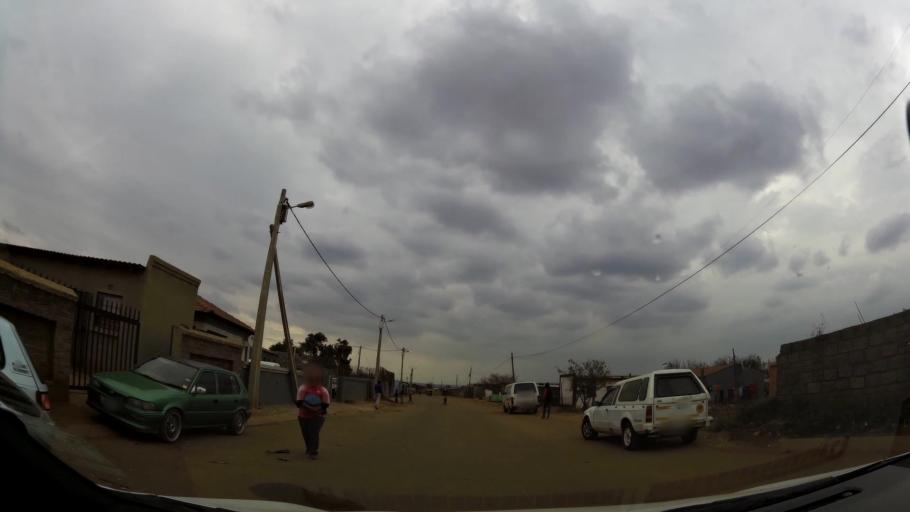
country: ZA
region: Gauteng
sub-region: Ekurhuleni Metropolitan Municipality
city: Germiston
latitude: -26.3924
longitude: 28.1383
